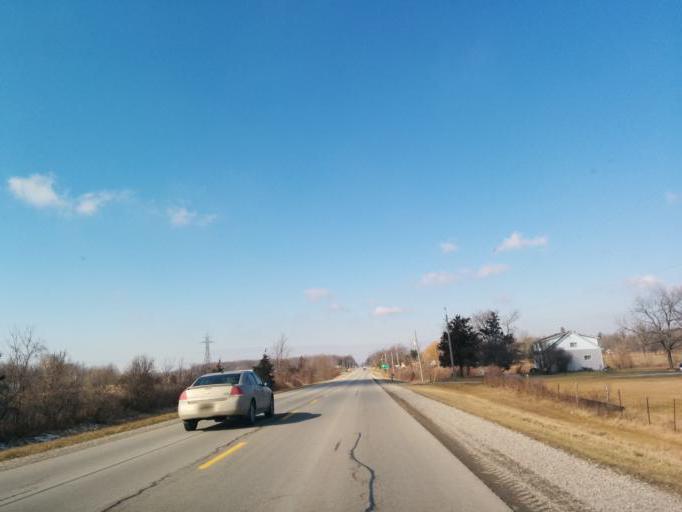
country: CA
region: Ontario
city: Brantford
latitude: 43.0094
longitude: -80.1803
